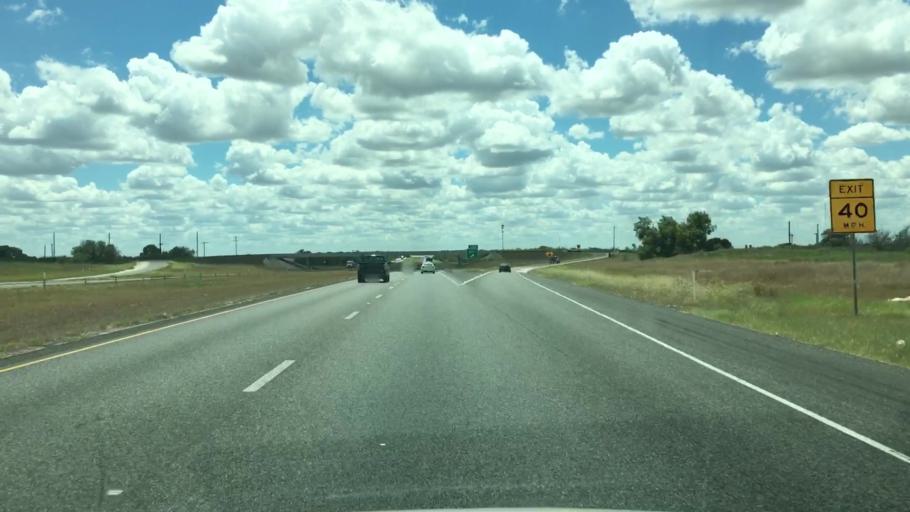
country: US
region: Texas
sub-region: Bexar County
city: Elmendorf
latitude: 29.1448
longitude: -98.4286
